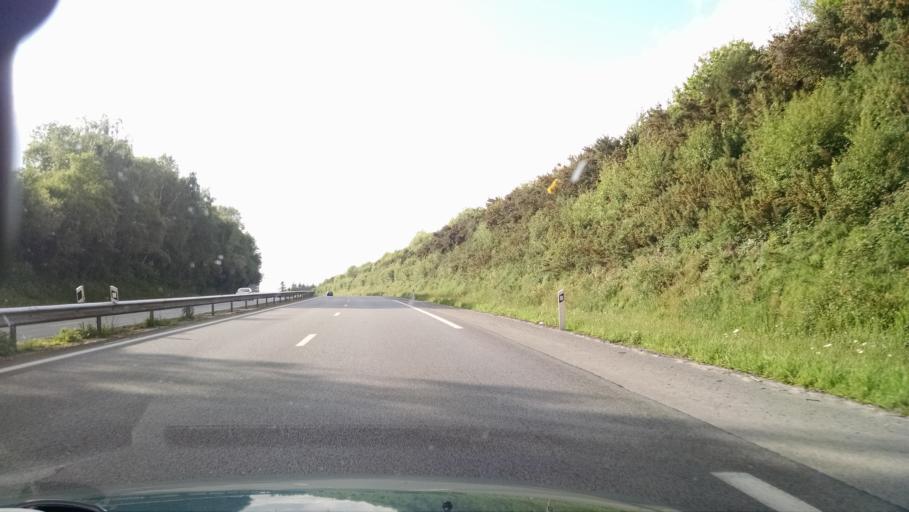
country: FR
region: Brittany
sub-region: Departement du Finistere
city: Taule
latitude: 48.5871
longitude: -3.8799
